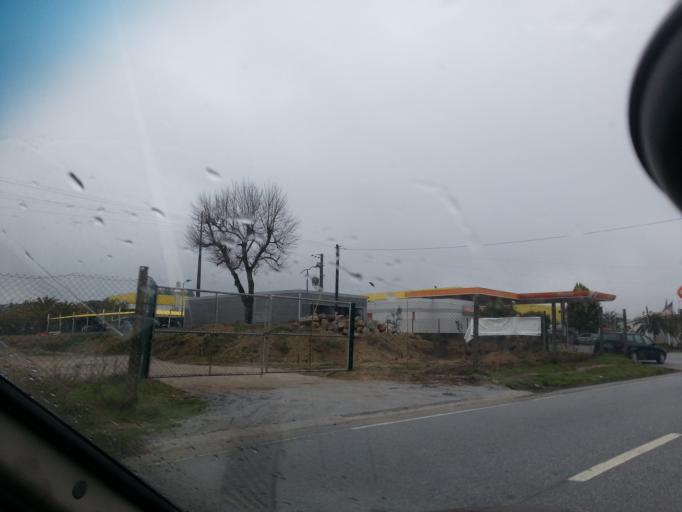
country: PT
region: Viseu
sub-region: Viseu
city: Rio de Loba
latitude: 40.6422
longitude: -7.8626
